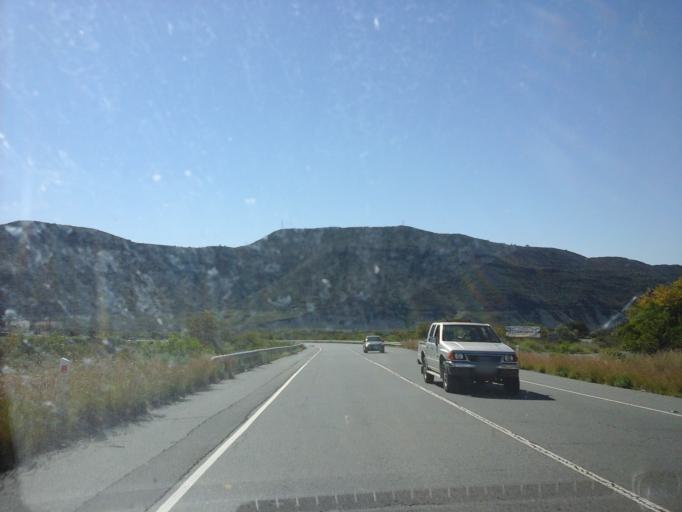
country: CY
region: Limassol
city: Sotira
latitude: 34.7636
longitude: 32.9229
